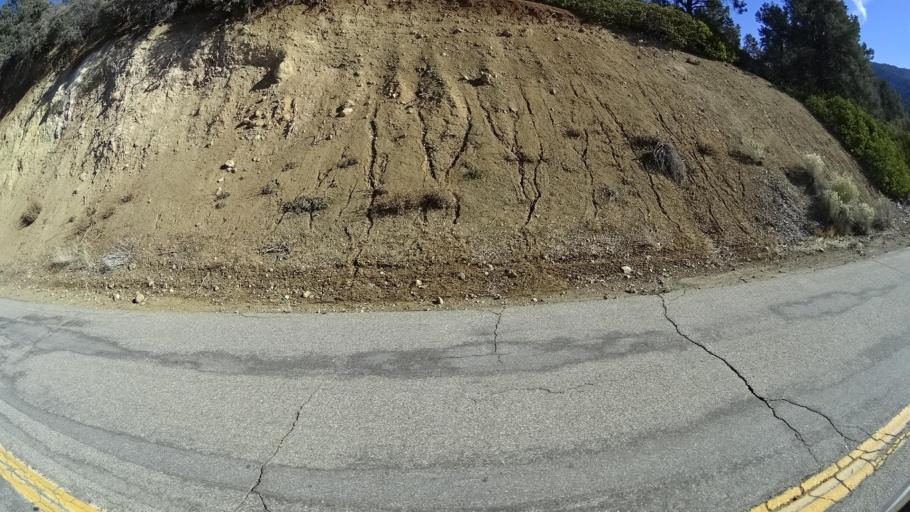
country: US
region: California
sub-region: Kern County
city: Pine Mountain Club
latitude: 34.8641
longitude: -119.2296
